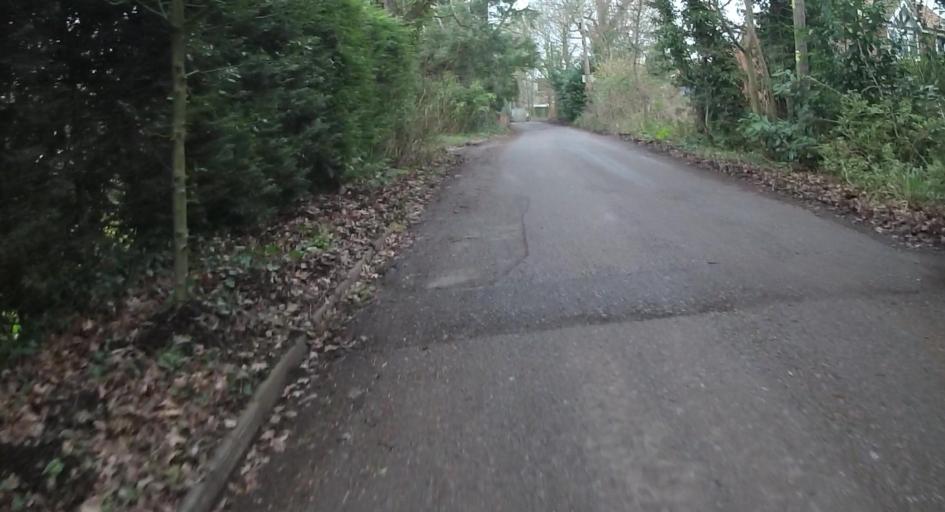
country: GB
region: England
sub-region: Wokingham
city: Barkham
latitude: 51.3883
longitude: -0.8596
